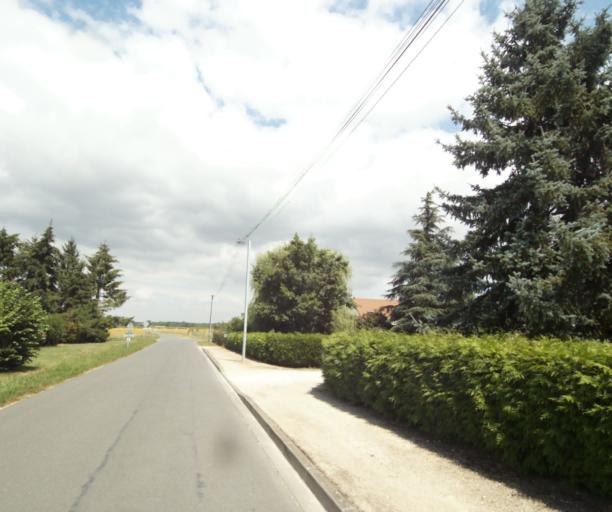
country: FR
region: Centre
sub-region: Departement du Loiret
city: Mardie
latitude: 47.8768
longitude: 2.0450
